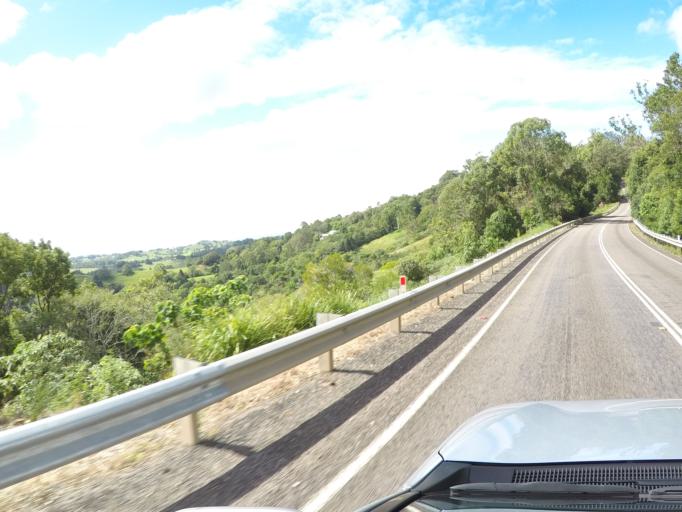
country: AU
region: Queensland
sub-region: Sunshine Coast
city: Nambour
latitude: -26.6419
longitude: 152.8715
